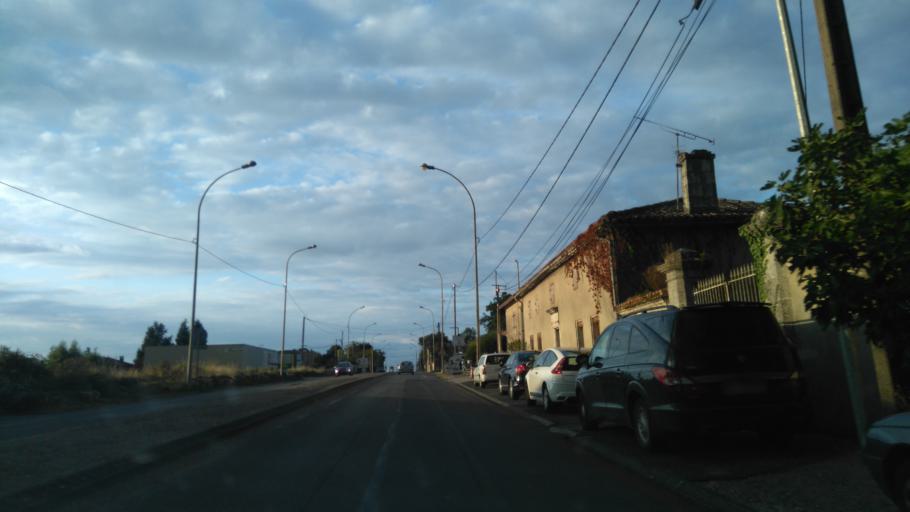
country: FR
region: Poitou-Charentes
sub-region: Departement de la Charente
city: Gond-Pontouvre
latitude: 45.7020
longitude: 0.1818
